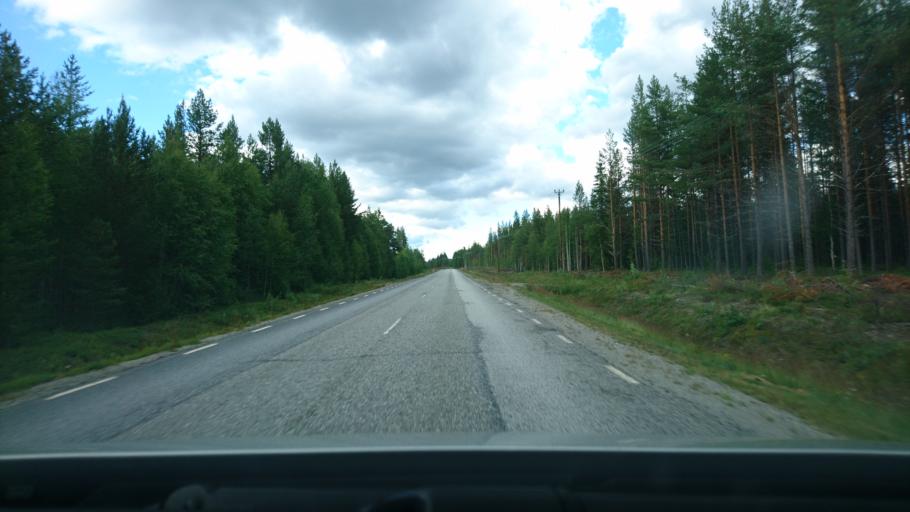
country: SE
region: Vaesterbotten
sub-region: Asele Kommun
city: Asele
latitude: 63.9254
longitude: 17.2583
